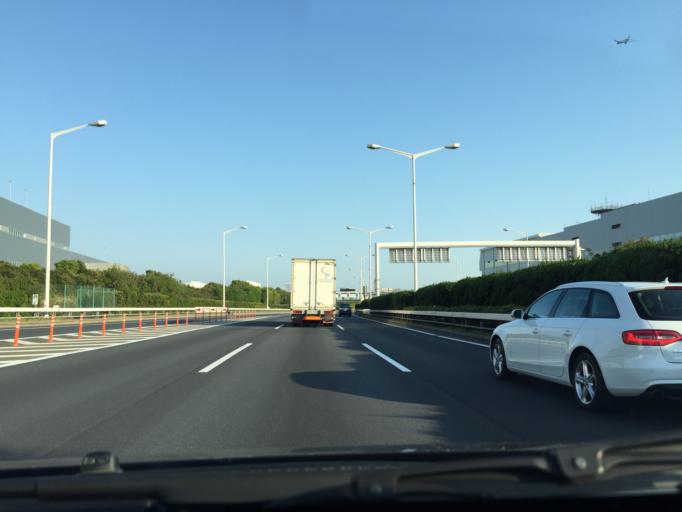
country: JP
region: Kanagawa
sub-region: Kawasaki-shi
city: Kawasaki
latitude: 35.5394
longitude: 139.7939
